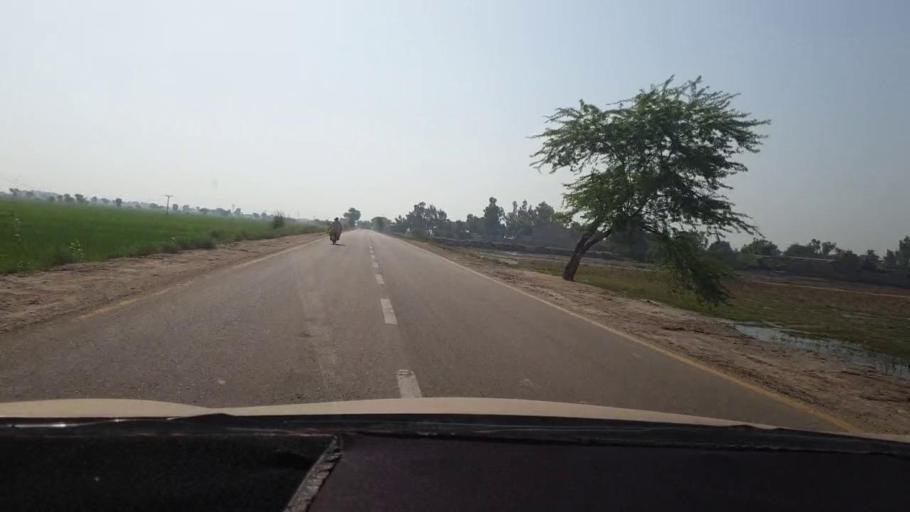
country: PK
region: Sindh
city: Miro Khan
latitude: 27.7244
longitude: 68.1386
